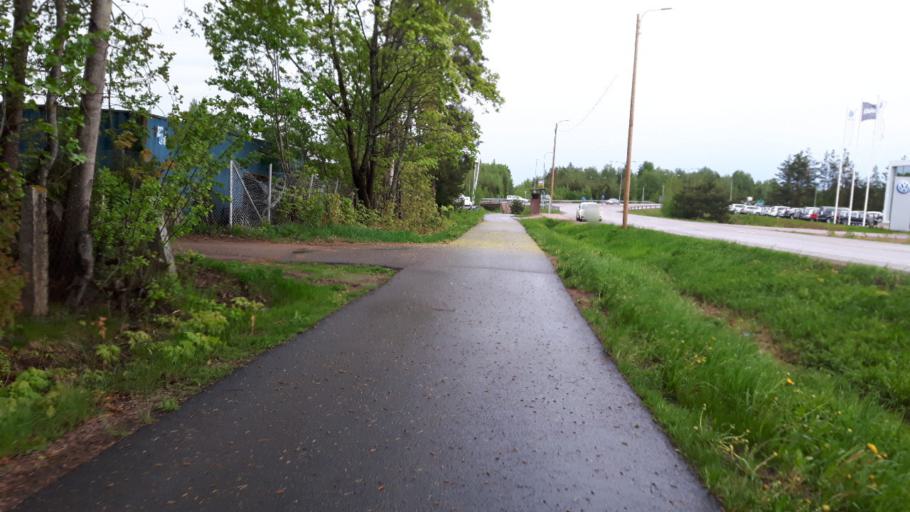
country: FI
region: Kymenlaakso
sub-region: Kotka-Hamina
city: Karhula
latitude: 60.5406
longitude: 26.9715
